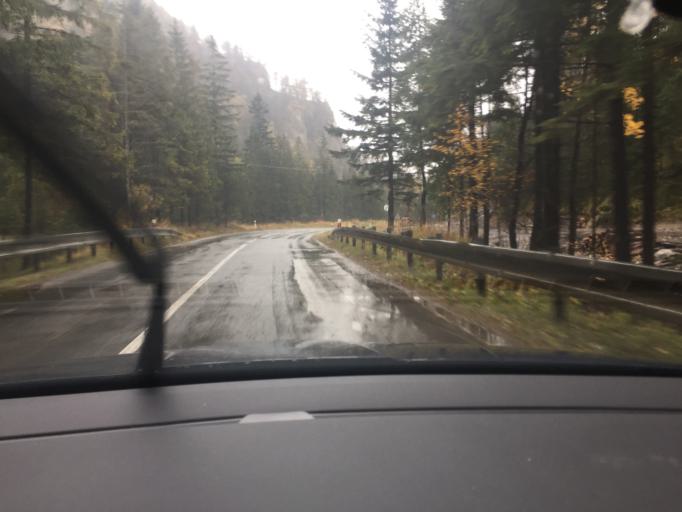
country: SK
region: Presovsky
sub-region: Okres Poprad
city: Zdiar
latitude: 49.2371
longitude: 20.3125
